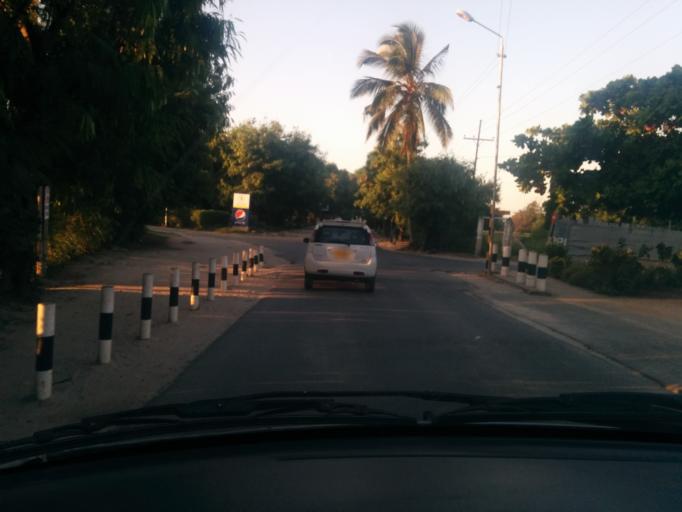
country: TZ
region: Dar es Salaam
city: Dar es Salaam
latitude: -6.8106
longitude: 39.2909
